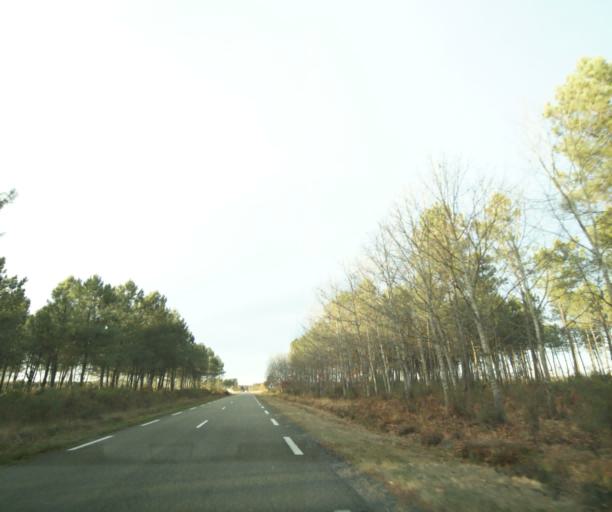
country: FR
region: Aquitaine
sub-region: Departement des Landes
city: Gabarret
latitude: 44.1459
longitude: -0.1244
